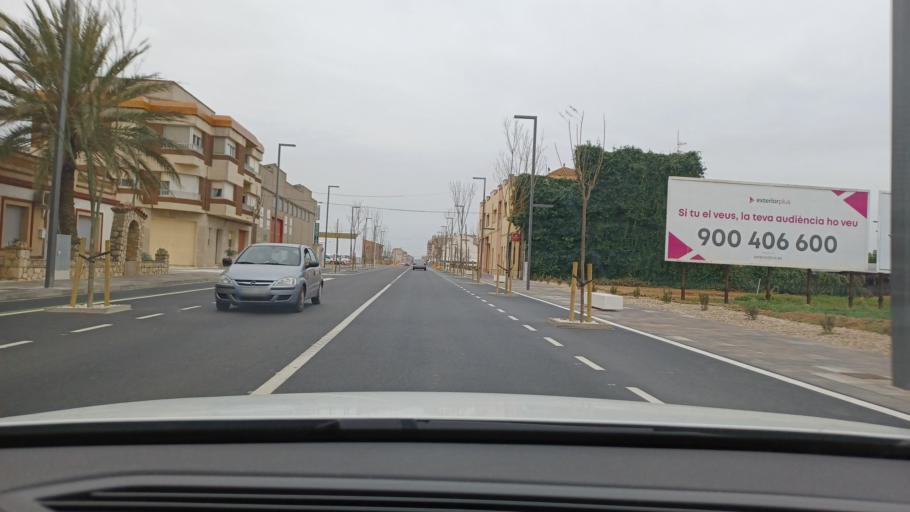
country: ES
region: Catalonia
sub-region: Provincia de Tarragona
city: Amposta
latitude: 40.7458
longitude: 0.6191
